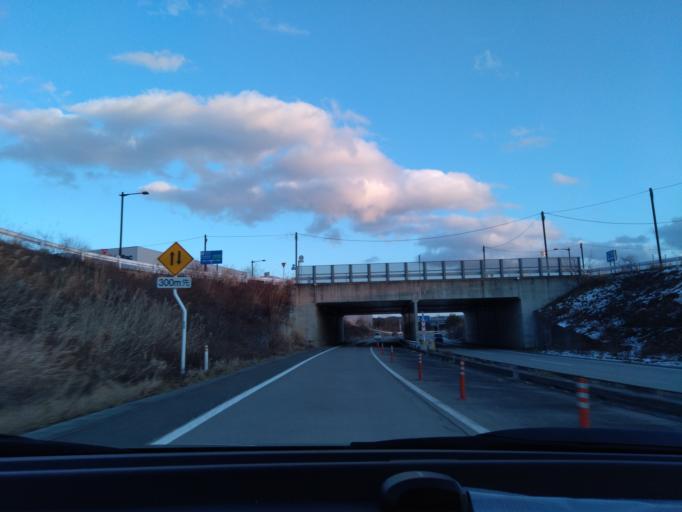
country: JP
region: Iwate
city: Hanamaki
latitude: 39.4107
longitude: 141.1335
